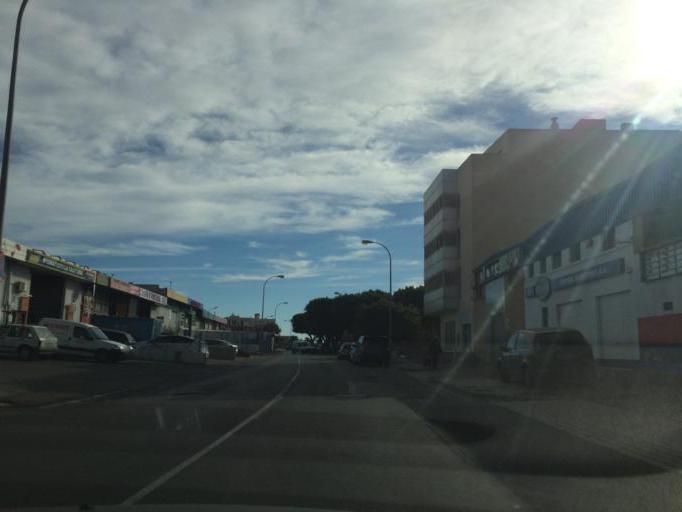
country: ES
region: Andalusia
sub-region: Provincia de Almeria
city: Almeria
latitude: 36.8381
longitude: -2.4428
